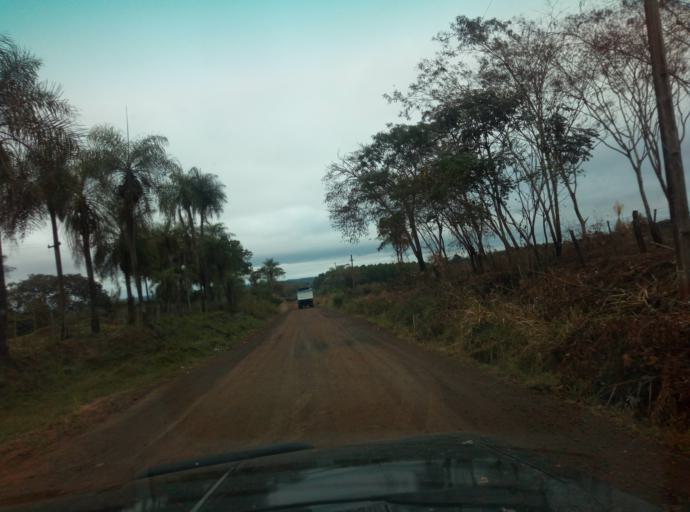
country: PY
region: Caaguazu
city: Carayao
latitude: -25.1902
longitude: -56.3813
